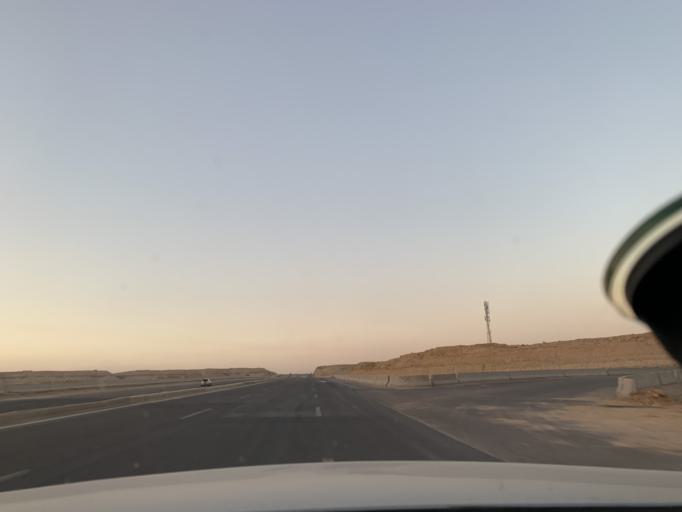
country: EG
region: Muhafazat al Qahirah
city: Halwan
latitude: 29.9390
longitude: 31.5304
